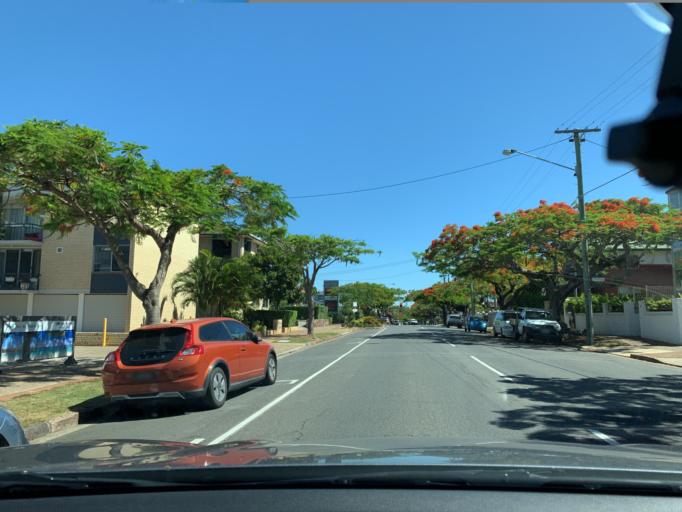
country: AU
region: Queensland
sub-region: Brisbane
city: Ascot
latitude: -27.4344
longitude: 153.0651
